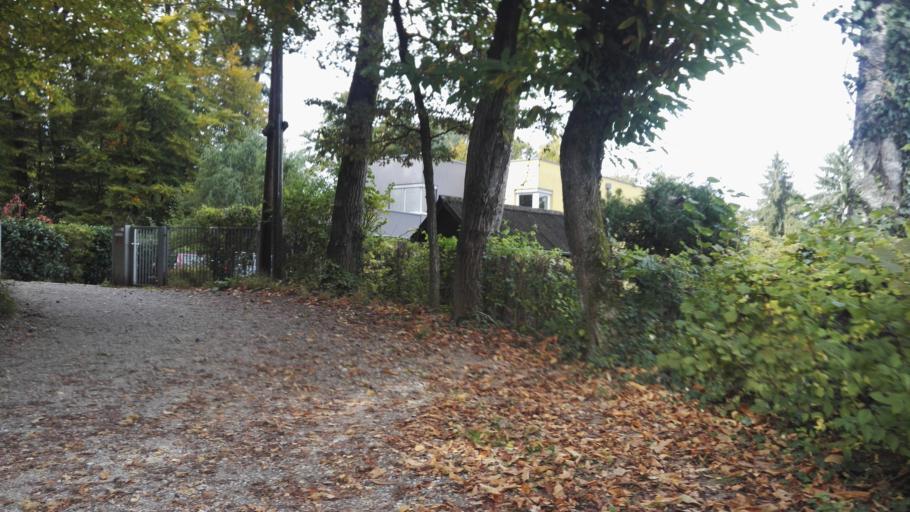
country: AT
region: Styria
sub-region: Graz Stadt
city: Mariatrost
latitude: 47.0948
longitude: 15.4731
